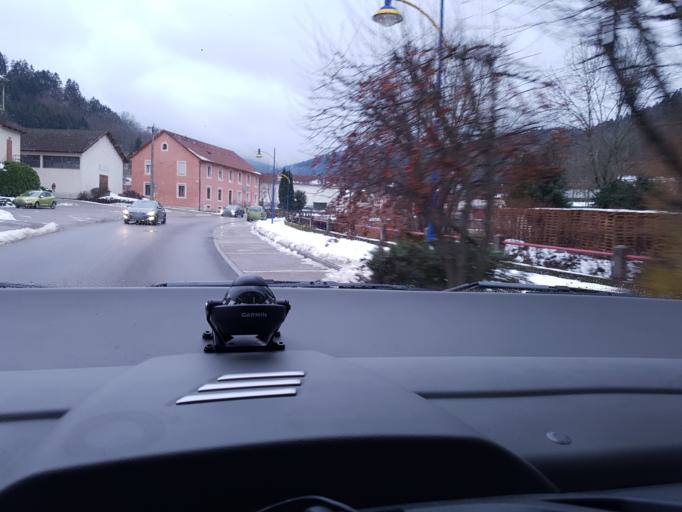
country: FR
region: Lorraine
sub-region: Departement des Vosges
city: Plainfaing
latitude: 48.1663
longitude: 7.0107
